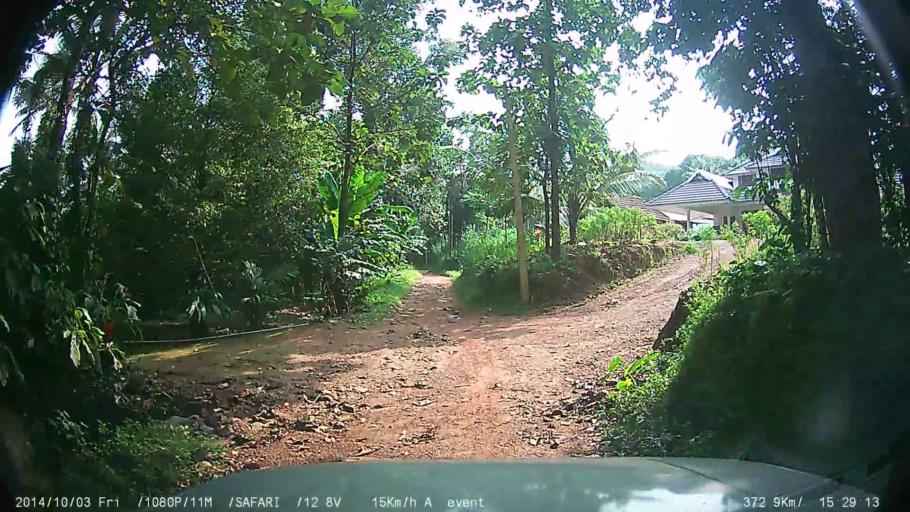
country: IN
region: Kerala
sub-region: Ernakulam
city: Muvattupuzha
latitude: 9.9265
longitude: 76.5660
